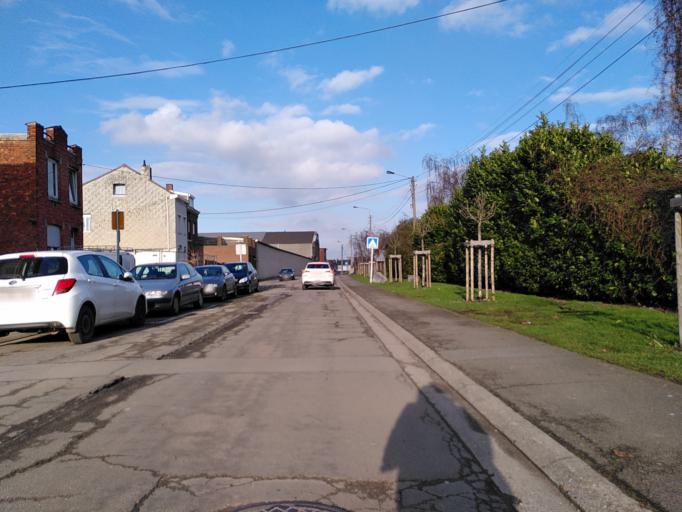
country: BE
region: Wallonia
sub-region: Province de Liege
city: Herstal
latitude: 50.6677
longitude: 5.6563
